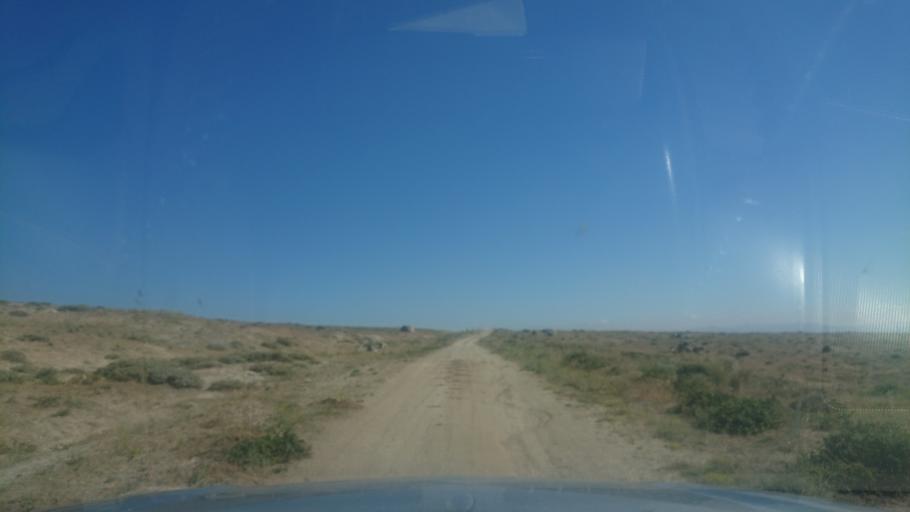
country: TR
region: Aksaray
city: Sariyahsi
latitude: 38.9228
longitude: 33.8522
